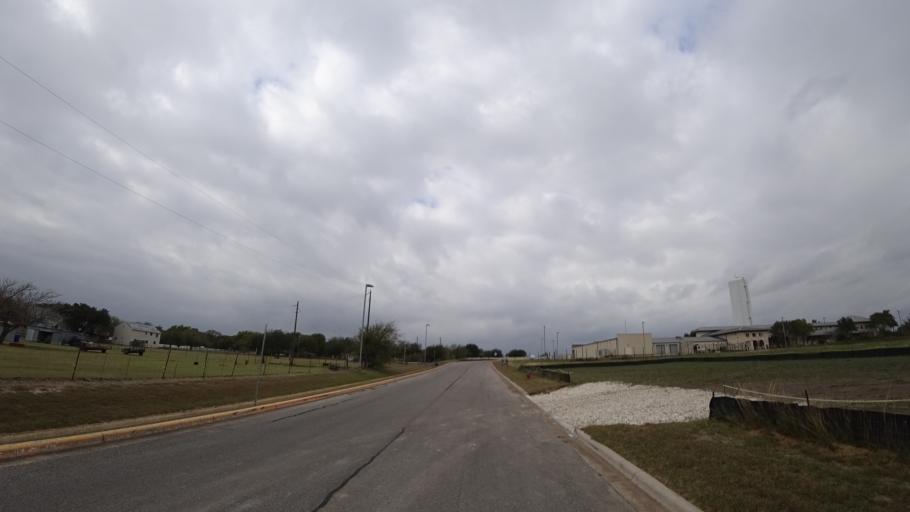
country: US
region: Texas
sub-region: Travis County
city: Pflugerville
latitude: 30.4491
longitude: -97.6076
